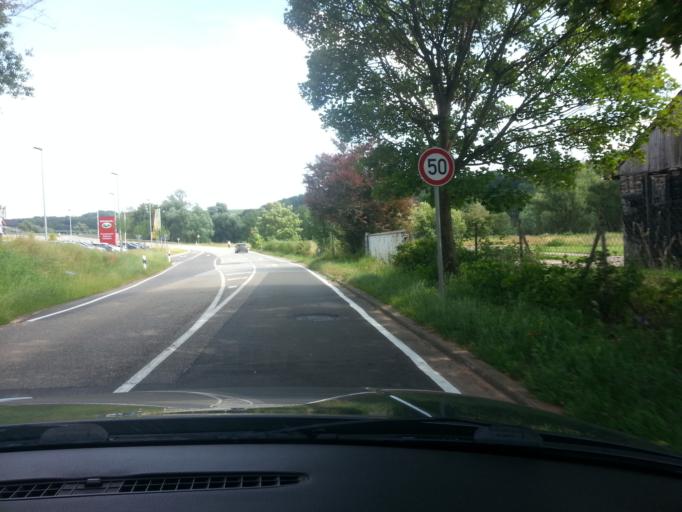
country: DE
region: Rheinland-Pfalz
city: Hornbach
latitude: 49.1877
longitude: 7.3737
